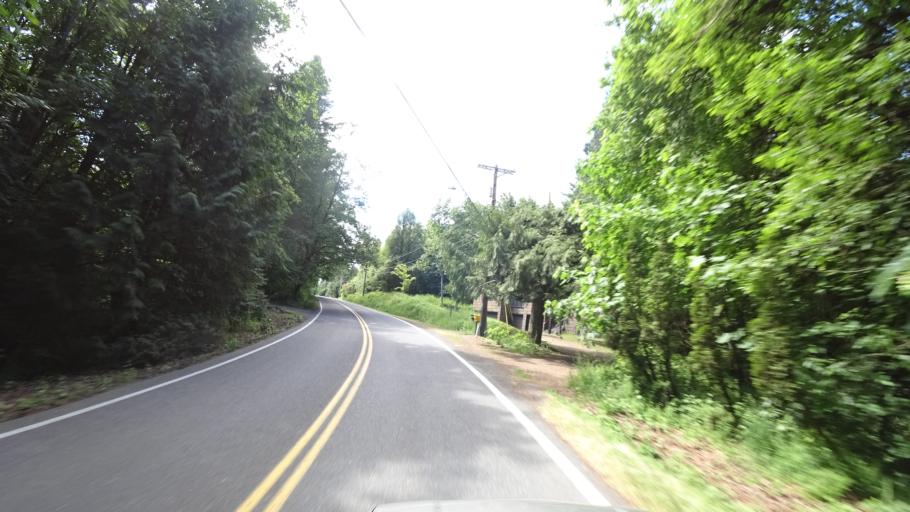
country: US
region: Oregon
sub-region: Washington County
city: Oak Hills
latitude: 45.5882
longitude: -122.8059
